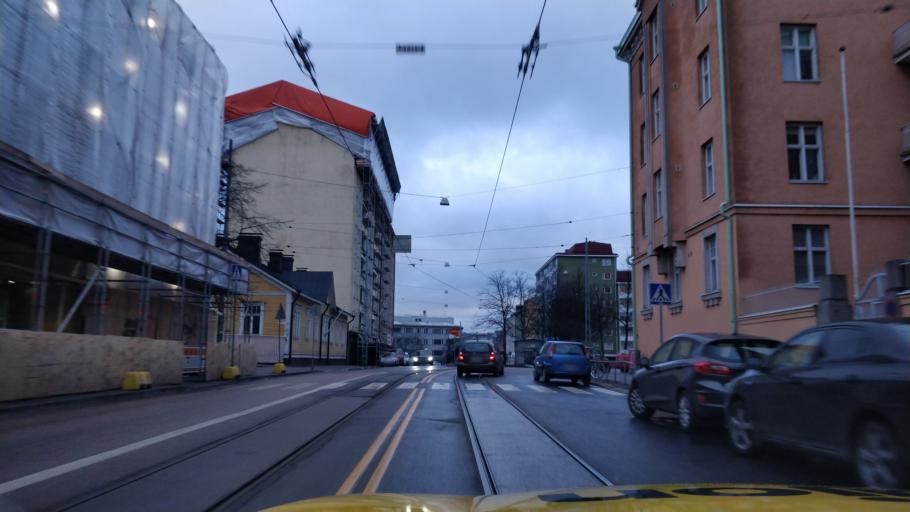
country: FI
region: Uusimaa
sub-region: Helsinki
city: Helsinki
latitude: 60.1902
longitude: 24.9466
